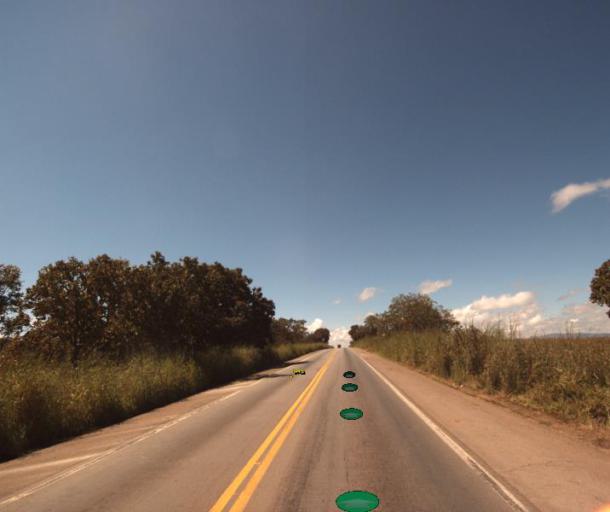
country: BR
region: Goias
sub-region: Jaragua
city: Jaragua
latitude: -15.6228
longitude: -49.3894
